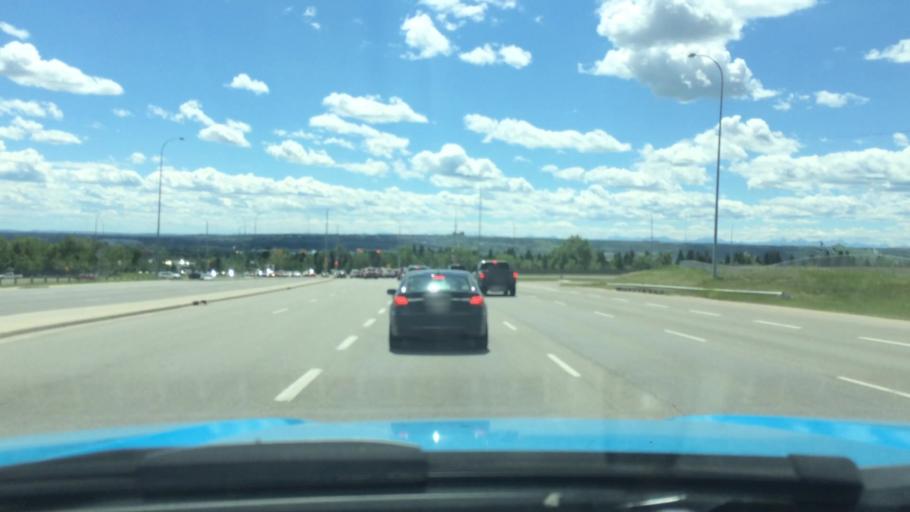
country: CA
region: Alberta
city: Calgary
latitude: 51.1108
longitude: -114.1389
